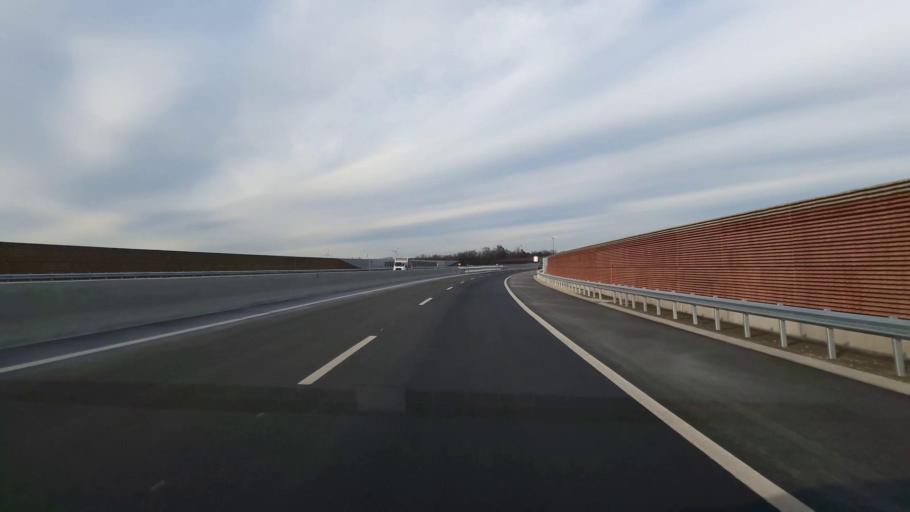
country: AT
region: Lower Austria
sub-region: Politischer Bezirk Mistelbach
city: Wilfersdorf
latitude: 48.5781
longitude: 16.6241
